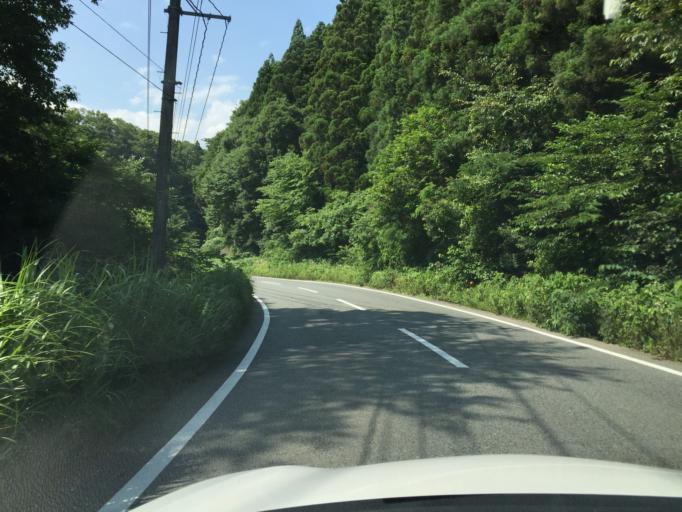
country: JP
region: Ibaraki
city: Kitaibaraki
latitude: 36.9138
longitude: 140.7451
